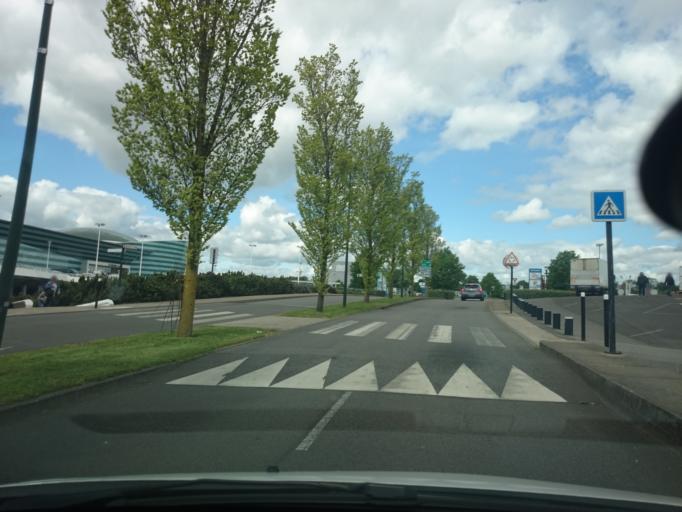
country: FR
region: Pays de la Loire
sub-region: Departement de la Loire-Atlantique
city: Saint-Herblain
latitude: 47.2238
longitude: -1.6297
